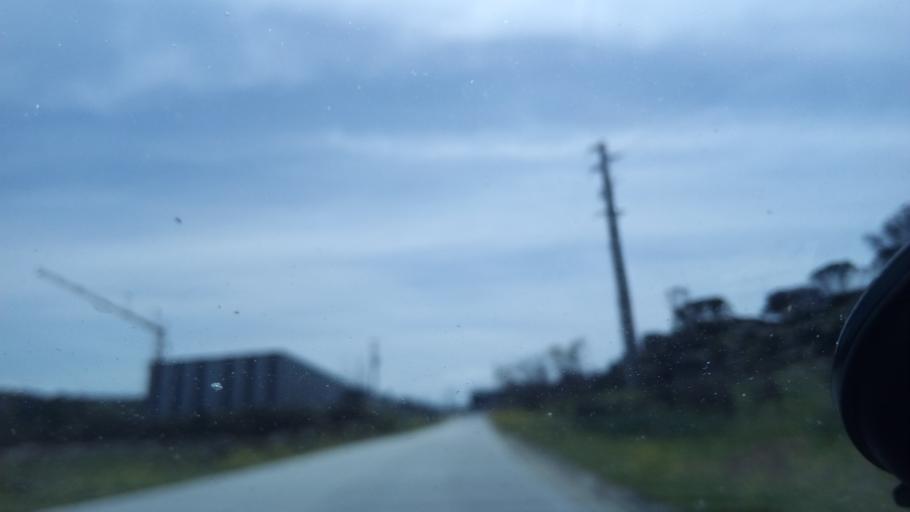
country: PT
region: Viseu
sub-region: Mangualde
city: Mangualde
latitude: 40.6115
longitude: -7.7882
